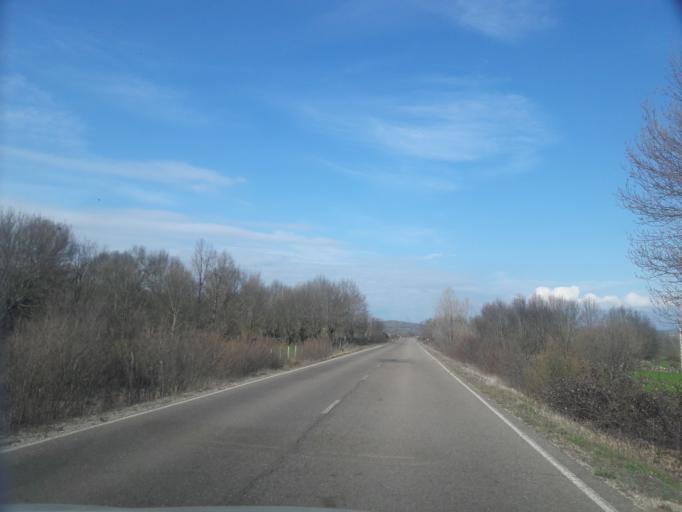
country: ES
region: Castille and Leon
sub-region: Provincia de Salamanca
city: Horcajo de Montemayor
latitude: 40.4225
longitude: -5.8737
